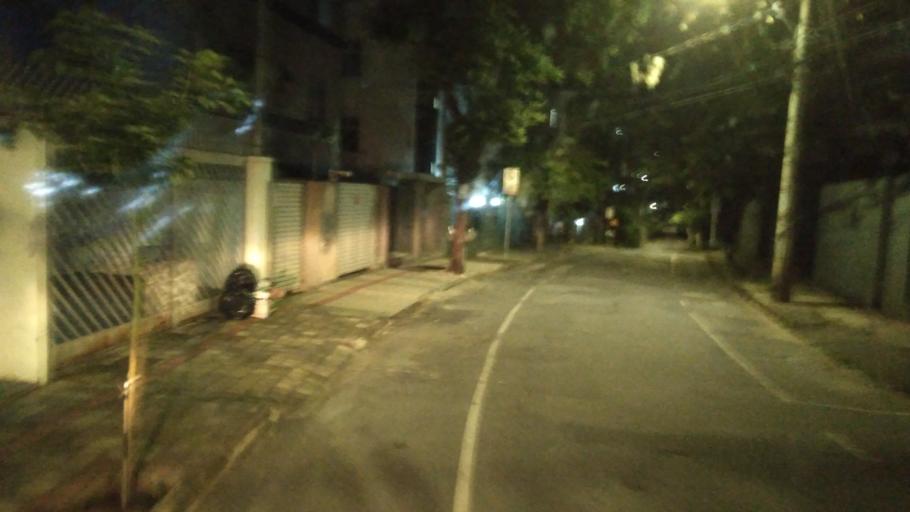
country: BR
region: Minas Gerais
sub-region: Belo Horizonte
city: Belo Horizonte
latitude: -19.8900
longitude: -43.9315
